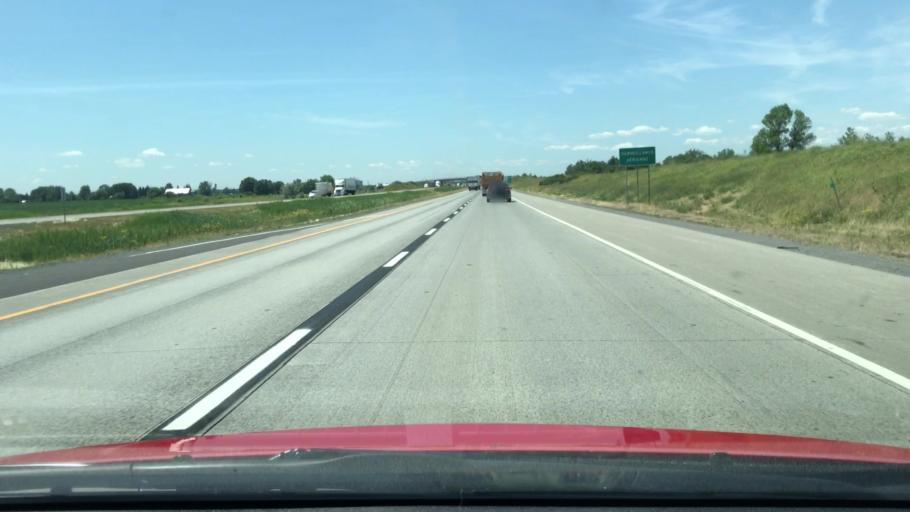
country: CA
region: Quebec
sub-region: Monteregie
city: Saint-Constant
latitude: 45.3573
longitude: -73.5672
